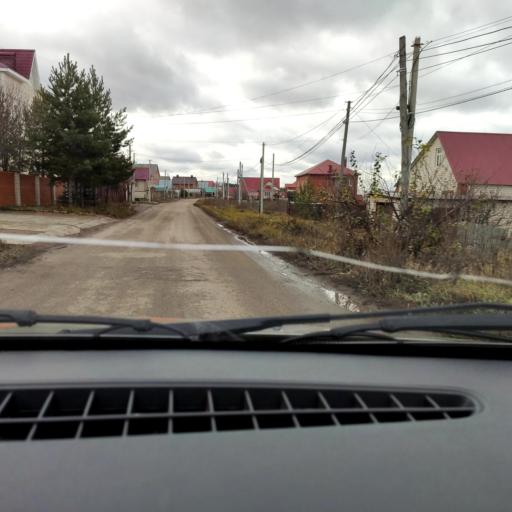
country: RU
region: Bashkortostan
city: Avdon
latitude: 54.4911
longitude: 55.8610
